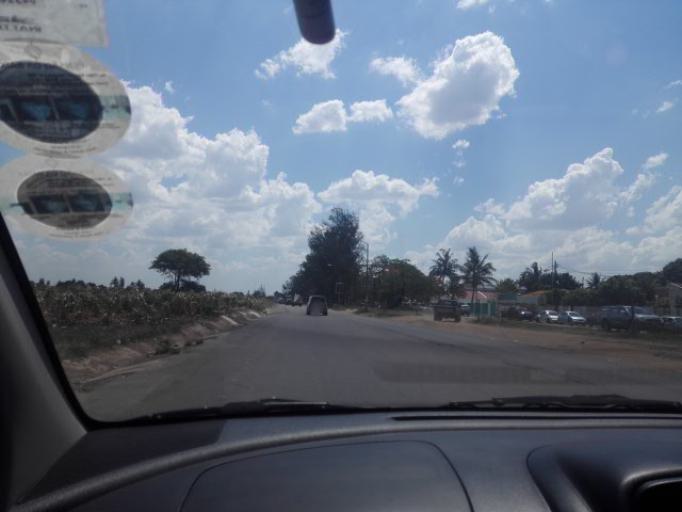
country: MZ
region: Maputo
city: Matola
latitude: -25.9550
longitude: 32.4574
